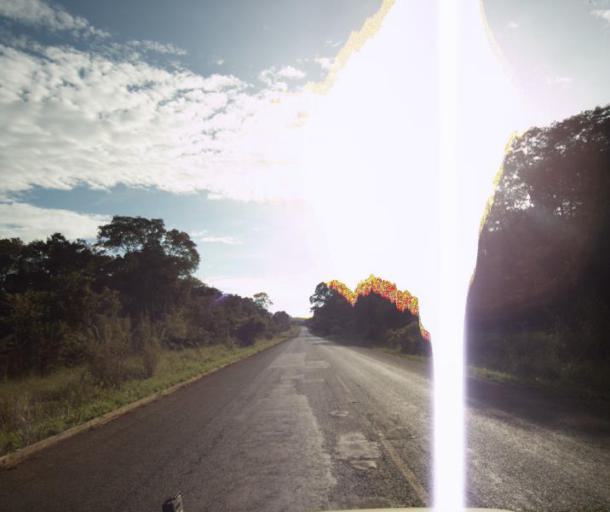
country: BR
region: Goias
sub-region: Pirenopolis
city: Pirenopolis
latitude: -15.6670
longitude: -48.6905
